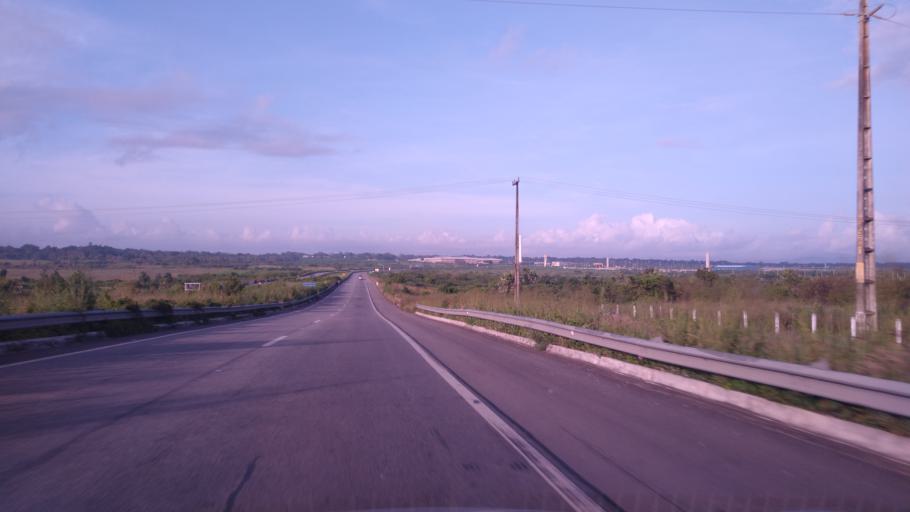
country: BR
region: Ceara
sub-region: Pacajus
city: Pacajus
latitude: -4.1558
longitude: -38.4818
